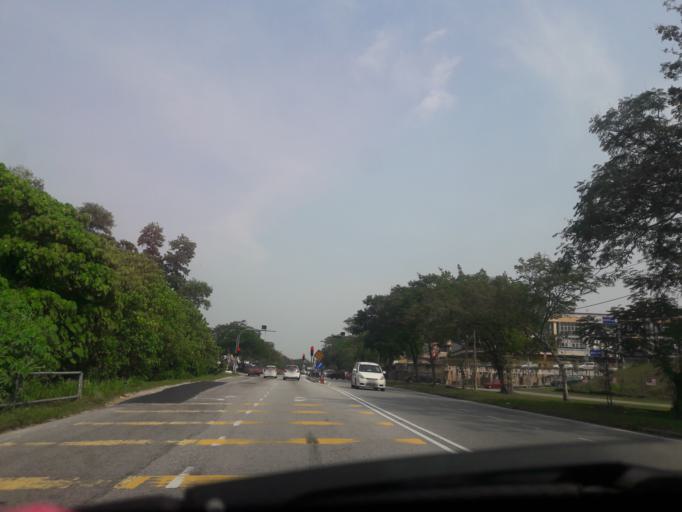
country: MY
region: Kedah
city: Kulim
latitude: 5.3682
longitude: 100.5445
